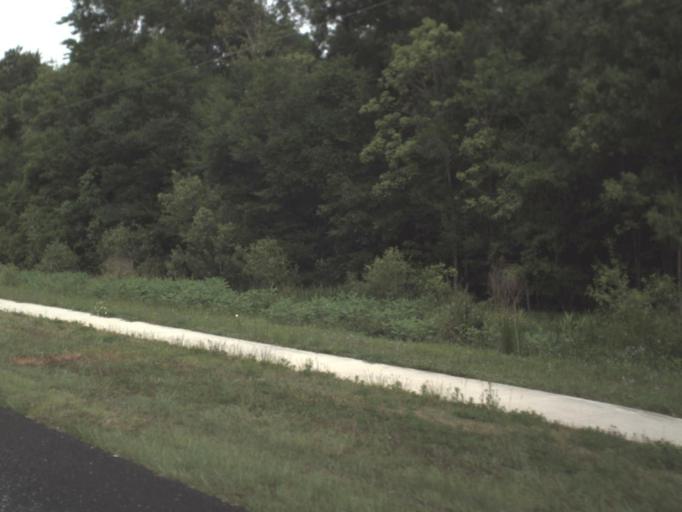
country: US
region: Florida
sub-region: Saint Johns County
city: Saint Augustine
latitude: 29.9156
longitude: -81.3743
